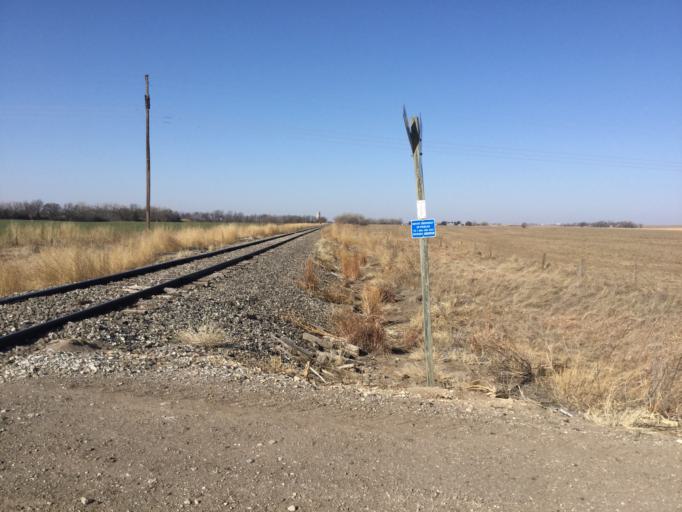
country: US
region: Kansas
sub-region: Rush County
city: La Crosse
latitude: 38.4689
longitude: -99.2352
